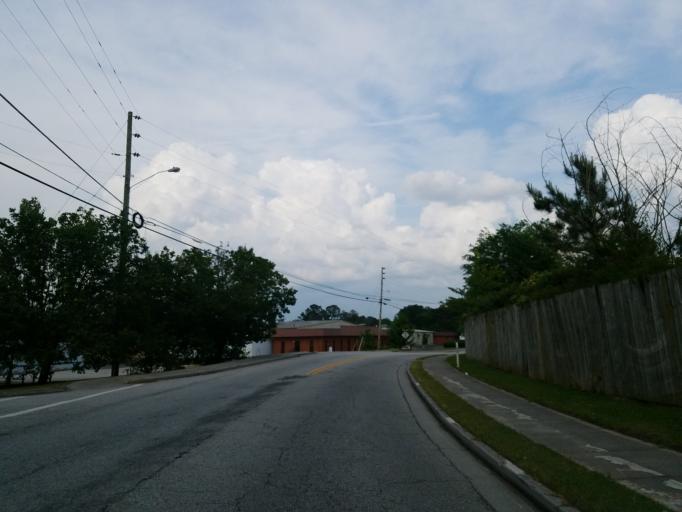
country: US
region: Georgia
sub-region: Cobb County
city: Austell
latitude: 33.8105
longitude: -84.6486
